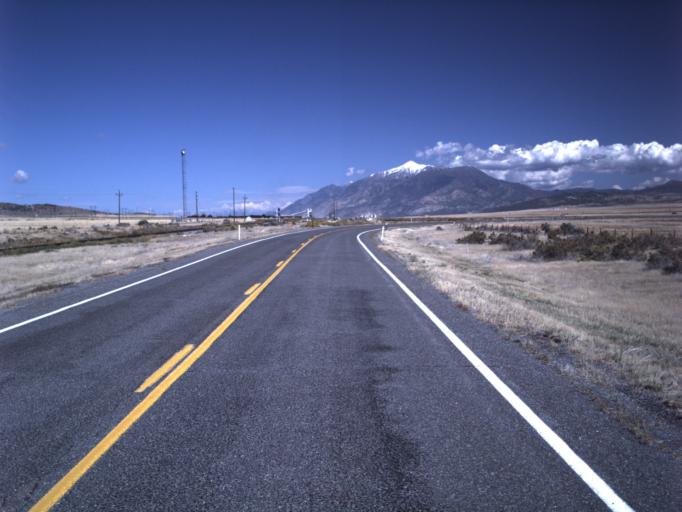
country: US
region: Utah
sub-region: Juab County
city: Nephi
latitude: 39.5545
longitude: -111.9215
